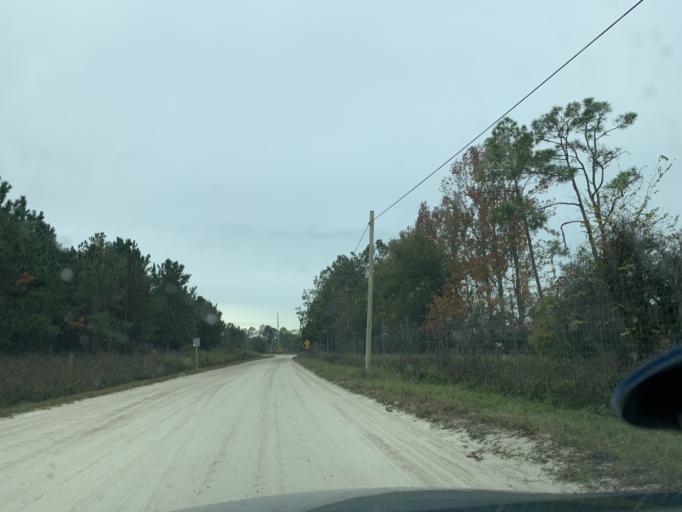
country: US
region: Florida
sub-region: Pasco County
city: Wesley Chapel
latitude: 28.2756
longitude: -82.3260
